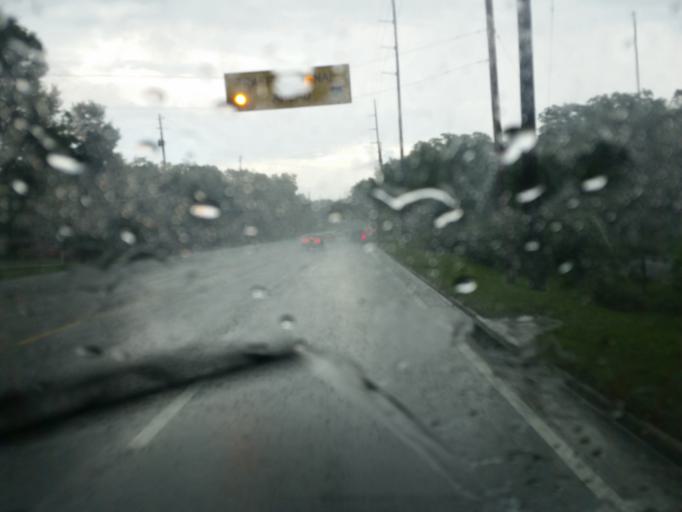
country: US
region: Alabama
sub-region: Mobile County
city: Prichard
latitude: 30.7195
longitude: -88.1413
